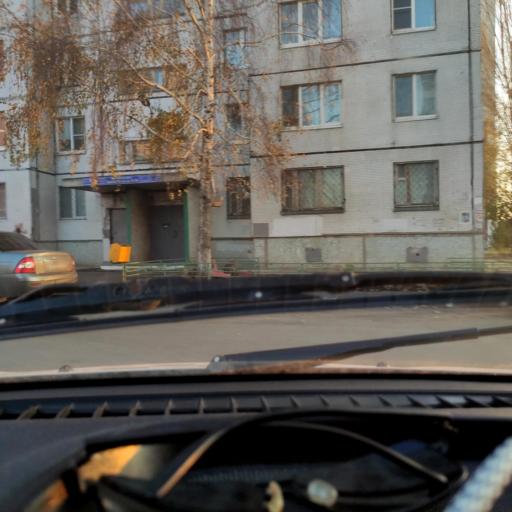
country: RU
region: Samara
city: Tol'yatti
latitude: 53.5401
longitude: 49.3950
